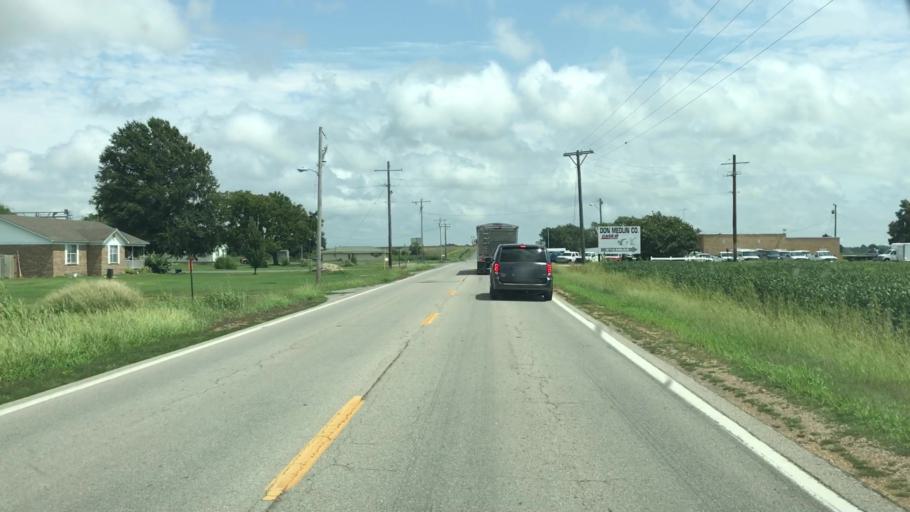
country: US
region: Missouri
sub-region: Pemiscot County
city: Caruthersville
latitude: 36.1762
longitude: -89.7010
